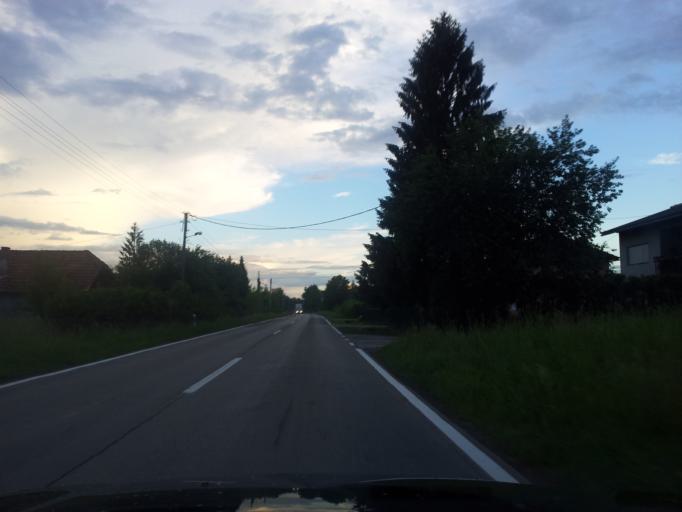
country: HR
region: Karlovacka
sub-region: Grad Karlovac
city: Karlovac
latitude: 45.5577
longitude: 15.5775
